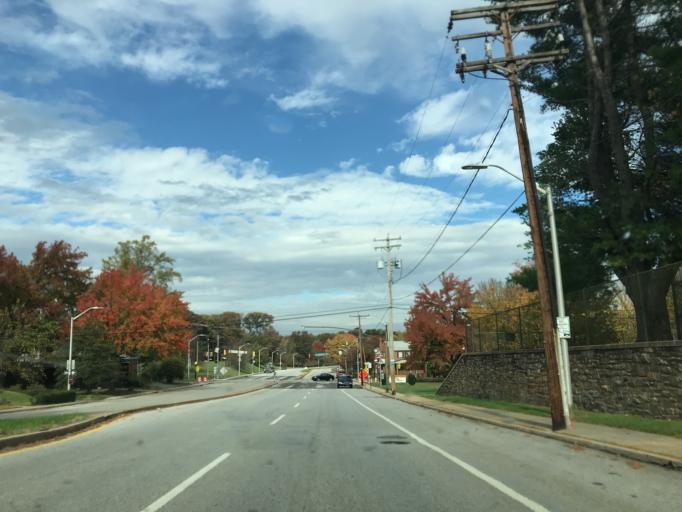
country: US
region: Maryland
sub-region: Baltimore County
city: Overlea
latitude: 39.3525
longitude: -76.5427
